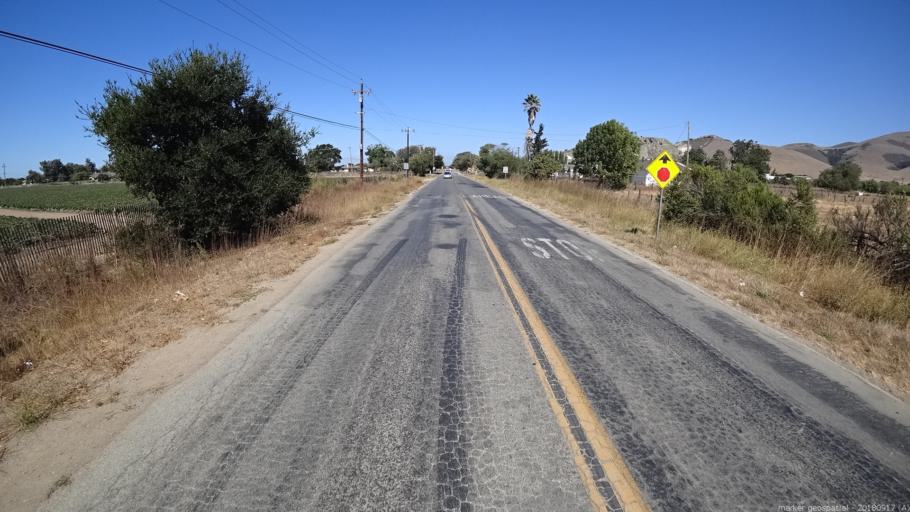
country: US
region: California
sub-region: Monterey County
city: Salinas
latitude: 36.7312
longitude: -121.5965
